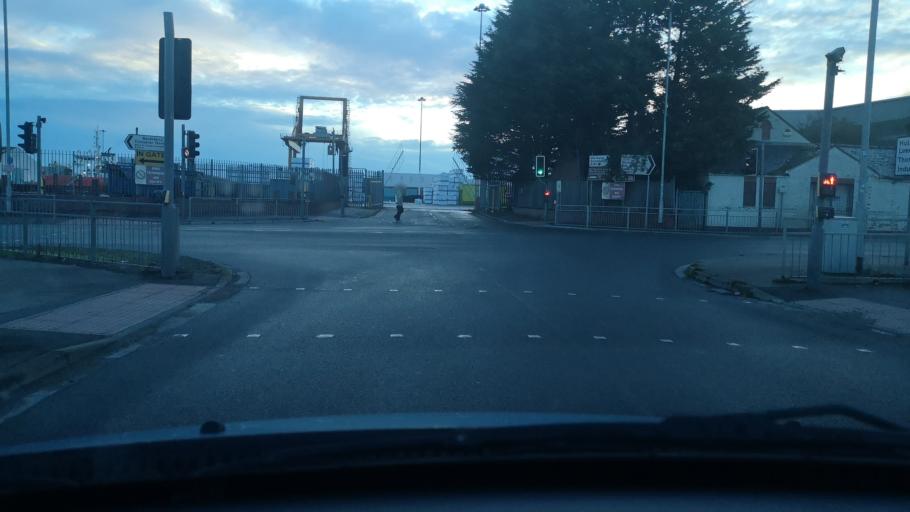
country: GB
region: England
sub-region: East Riding of Yorkshire
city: Goole
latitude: 53.6993
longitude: -0.8750
